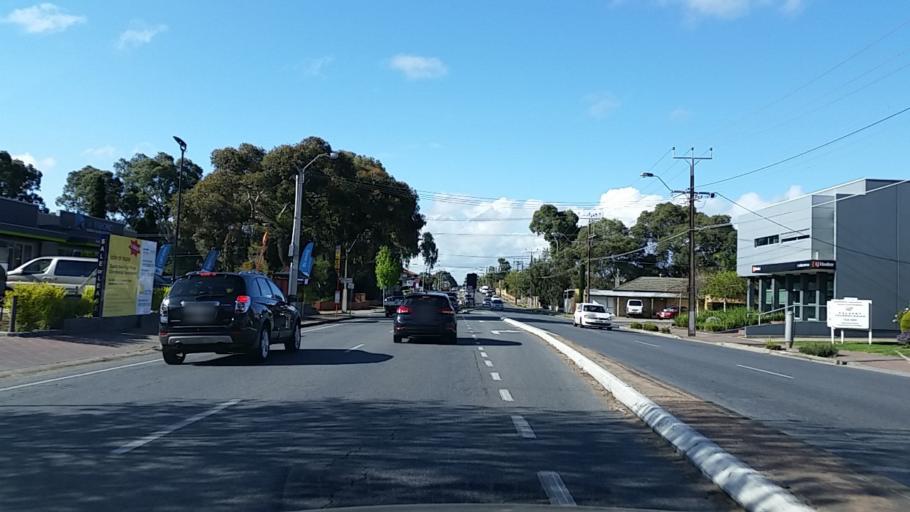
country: AU
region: South Australia
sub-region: Campbelltown
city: Hectorville
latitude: -34.8882
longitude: 138.6573
